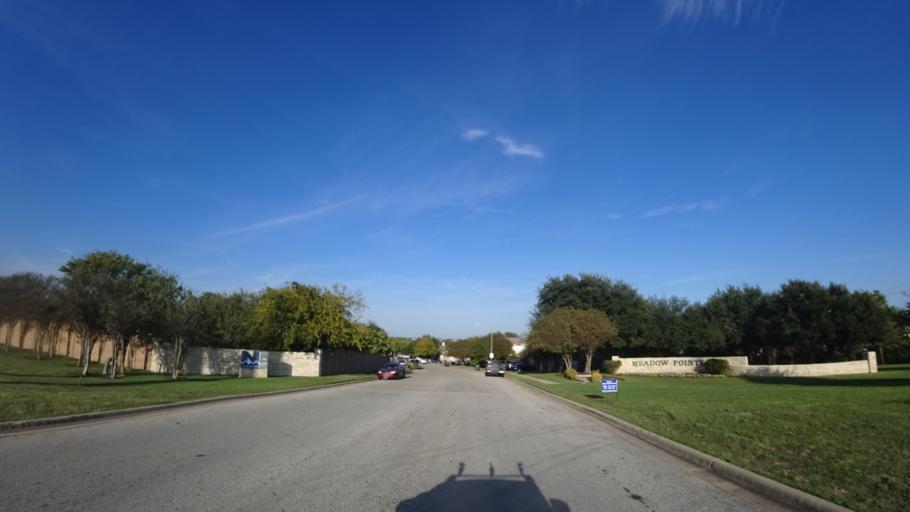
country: US
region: Texas
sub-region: Travis County
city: Wells Branch
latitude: 30.4157
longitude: -97.6554
